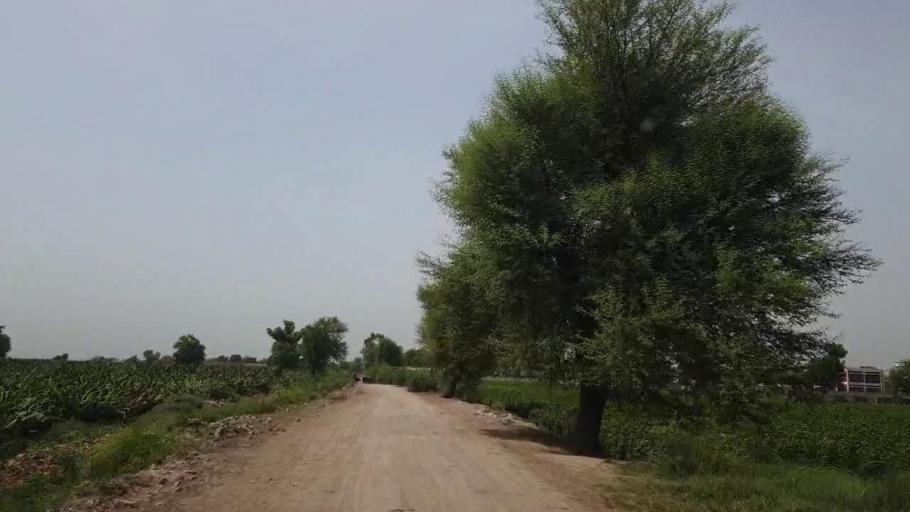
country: PK
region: Sindh
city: Sakrand
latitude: 26.1286
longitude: 68.2864
